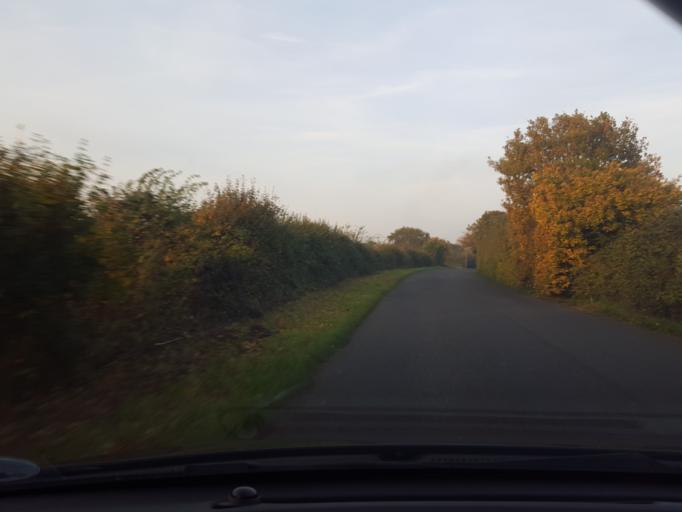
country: GB
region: England
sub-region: Essex
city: Saint Osyth
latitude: 51.8148
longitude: 1.0939
